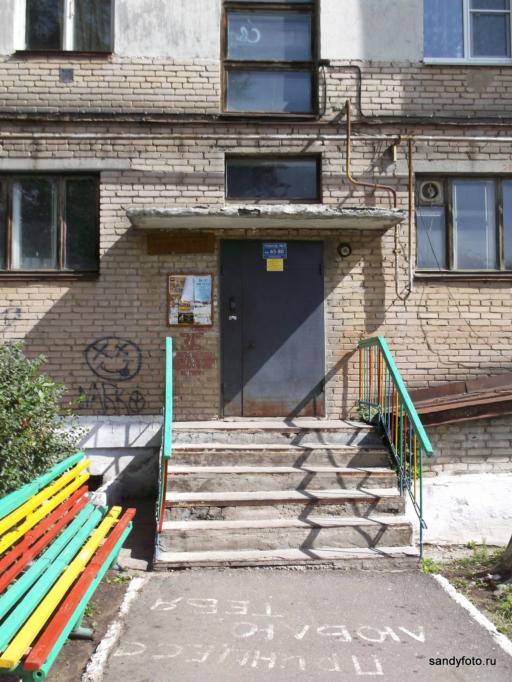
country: RU
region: Chelyabinsk
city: Troitsk
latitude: 54.0789
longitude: 61.5395
